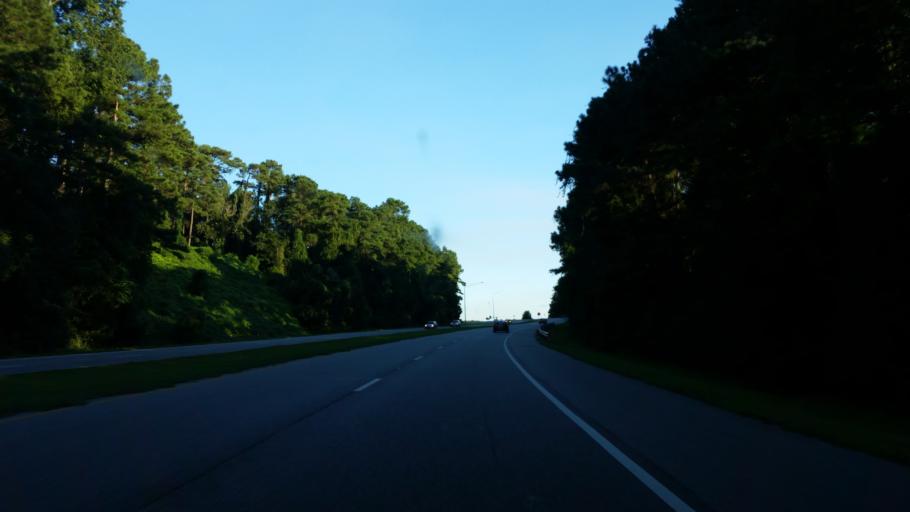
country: US
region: Alabama
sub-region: Baldwin County
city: Spanish Fort
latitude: 30.6616
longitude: -87.9136
